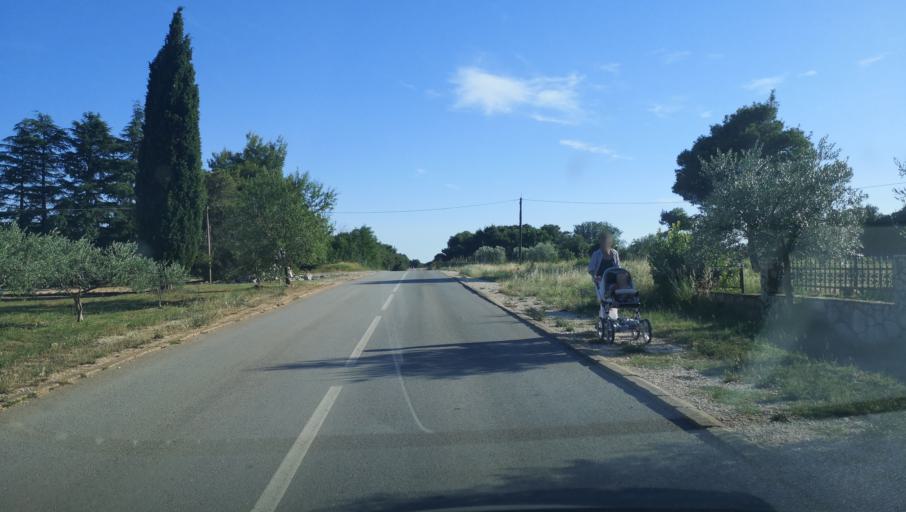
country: HR
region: Istarska
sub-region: Grad Rovinj
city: Rovinj
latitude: 45.0600
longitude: 13.6892
